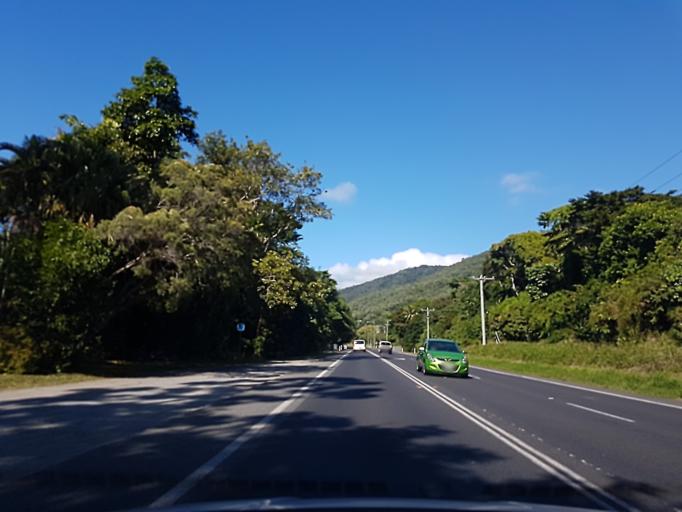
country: AU
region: Queensland
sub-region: Cairns
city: Palm Cove
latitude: -16.7483
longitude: 145.6628
